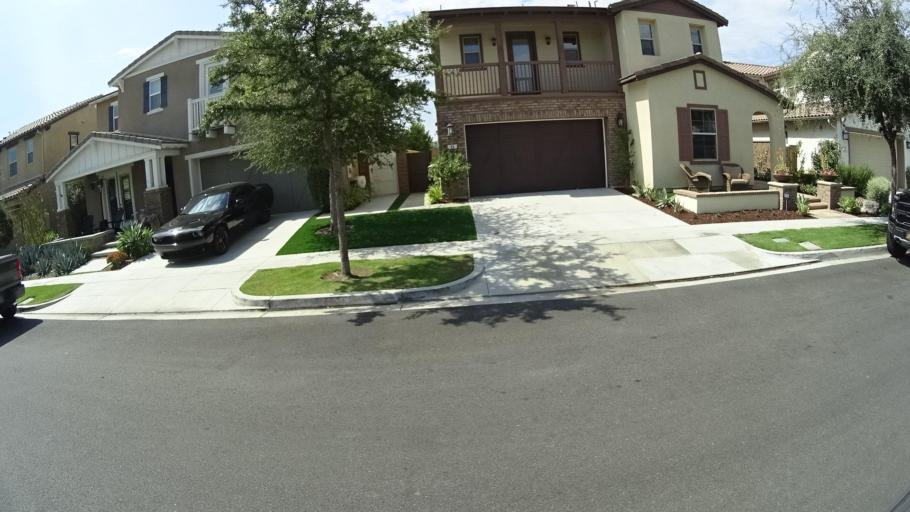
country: US
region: California
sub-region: Orange County
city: Ladera Ranch
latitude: 33.5305
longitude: -117.6024
